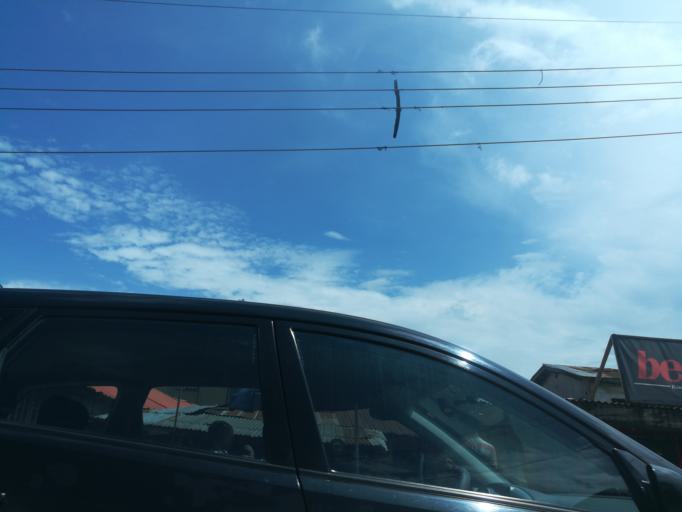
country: NG
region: Lagos
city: Agege
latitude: 6.6219
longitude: 3.3288
